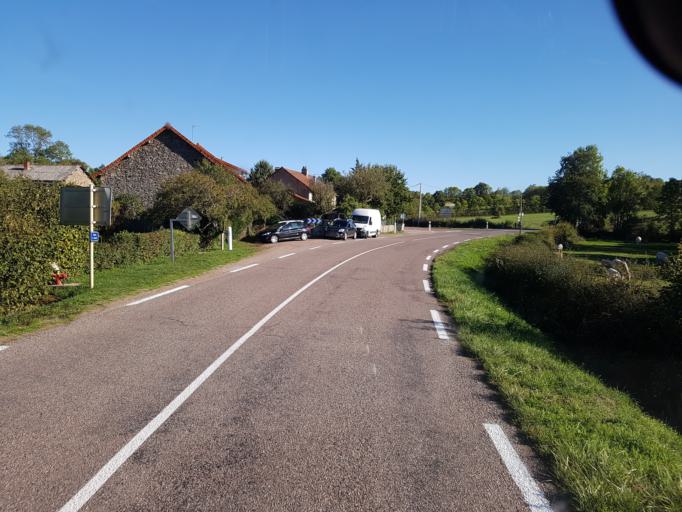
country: FR
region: Bourgogne
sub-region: Departement de Saone-et-Loire
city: Autun
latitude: 47.0602
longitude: 4.2611
